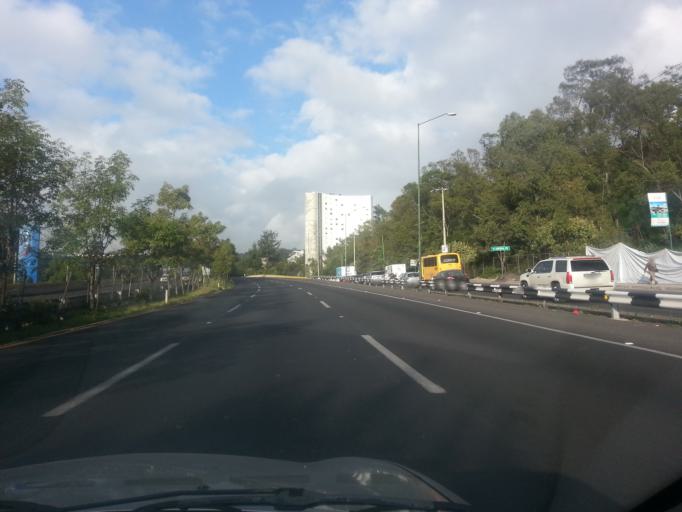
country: MX
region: Mexico City
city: Col. Bosques de las Lomas
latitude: 19.3766
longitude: -99.2584
